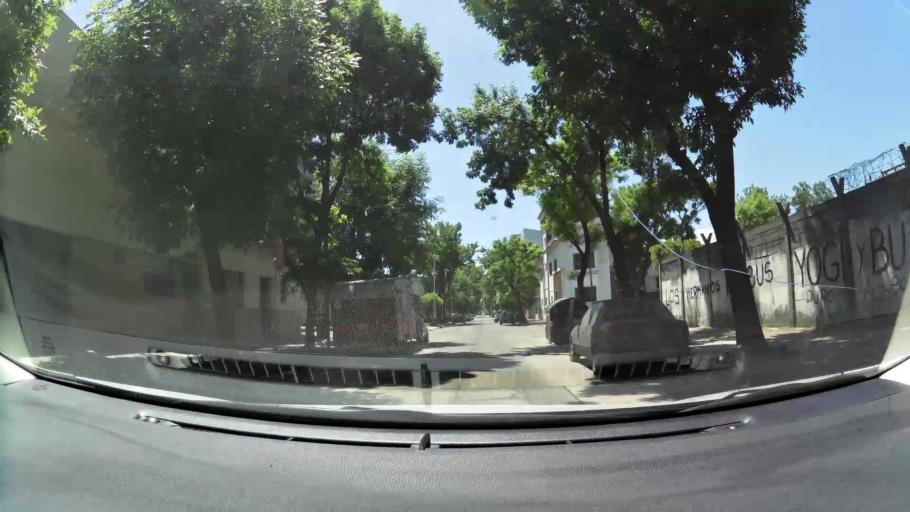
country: AR
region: Buenos Aires
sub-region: Partido de Avellaneda
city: Avellaneda
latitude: -34.6529
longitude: -58.3921
